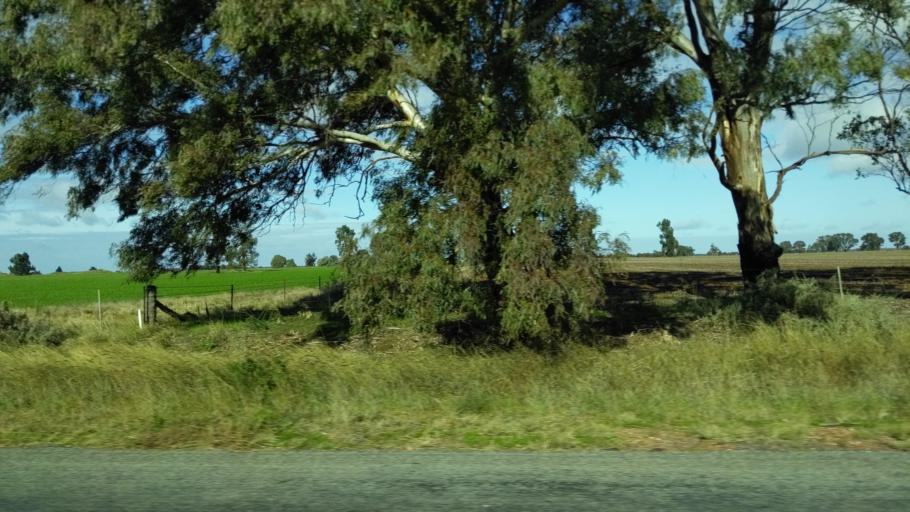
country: AU
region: New South Wales
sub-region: Narrandera
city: Narrandera
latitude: -34.7472
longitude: 146.8194
